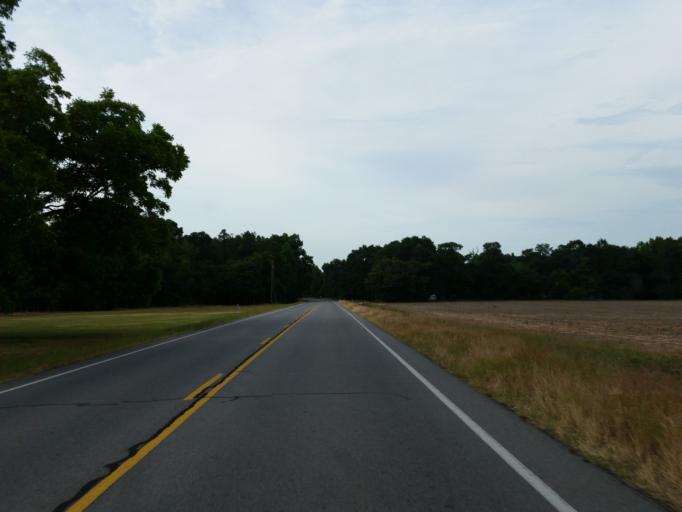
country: US
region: Georgia
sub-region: Dooly County
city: Unadilla
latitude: 32.2209
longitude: -83.7585
